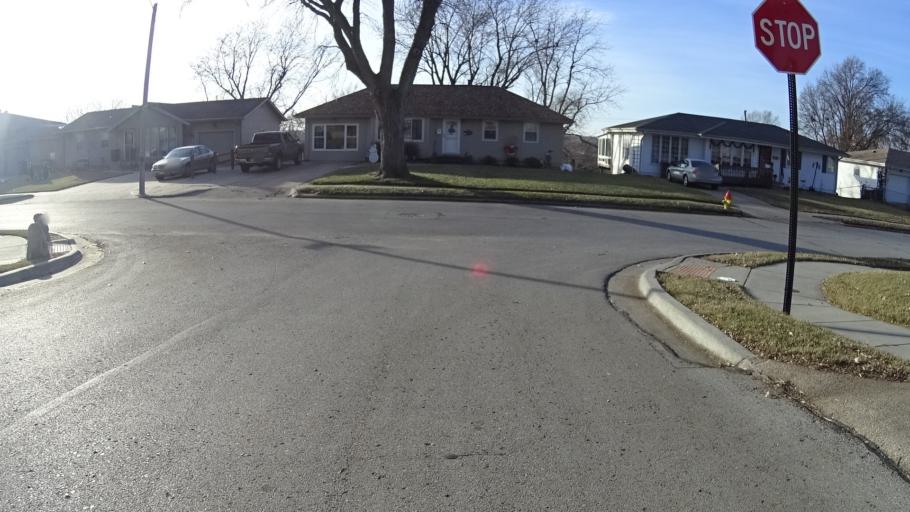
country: US
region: Nebraska
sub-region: Sarpy County
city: La Vista
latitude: 41.1889
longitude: -95.9967
